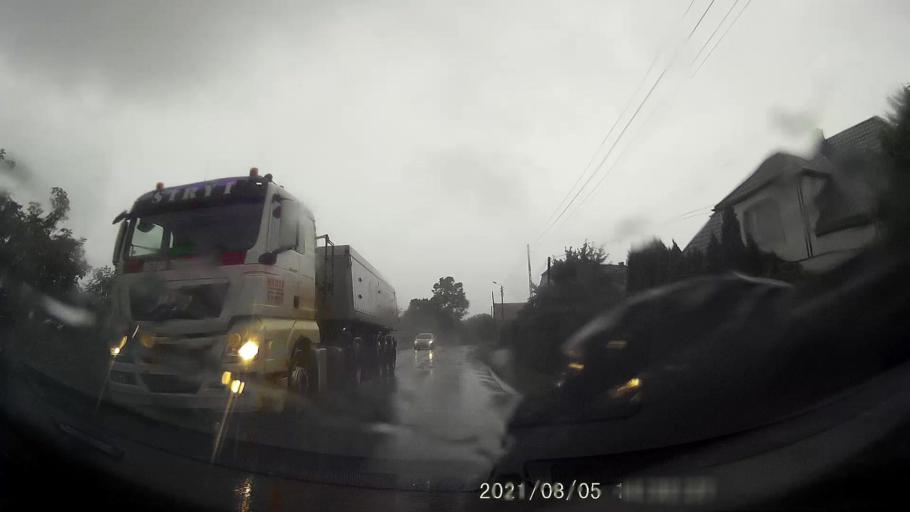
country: PL
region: Opole Voivodeship
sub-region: Powiat nyski
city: Korfantow
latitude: 50.4771
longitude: 17.6568
